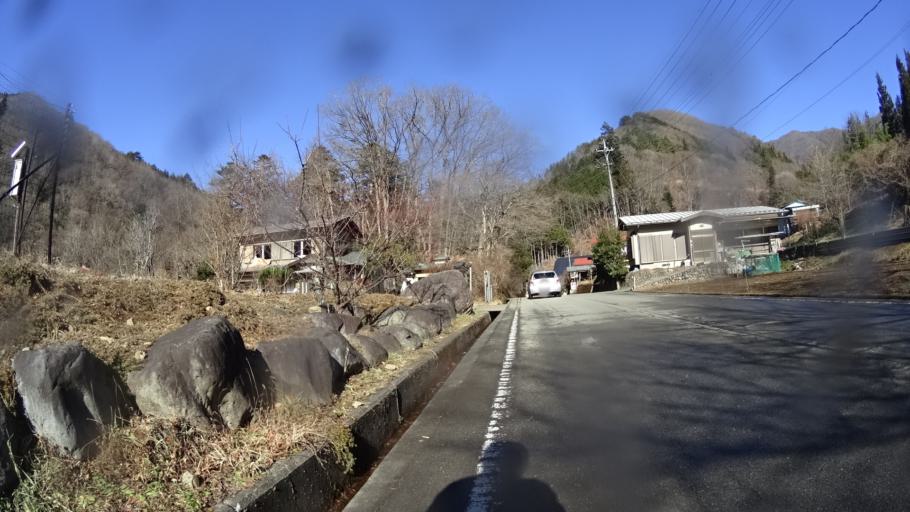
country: JP
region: Yamanashi
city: Otsuki
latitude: 35.7183
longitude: 138.9917
